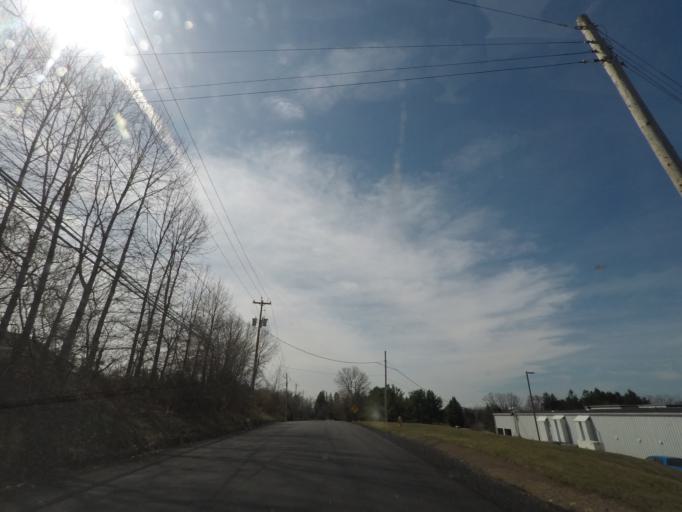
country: US
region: New York
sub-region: Saratoga County
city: Mechanicville
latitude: 42.8701
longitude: -73.7247
